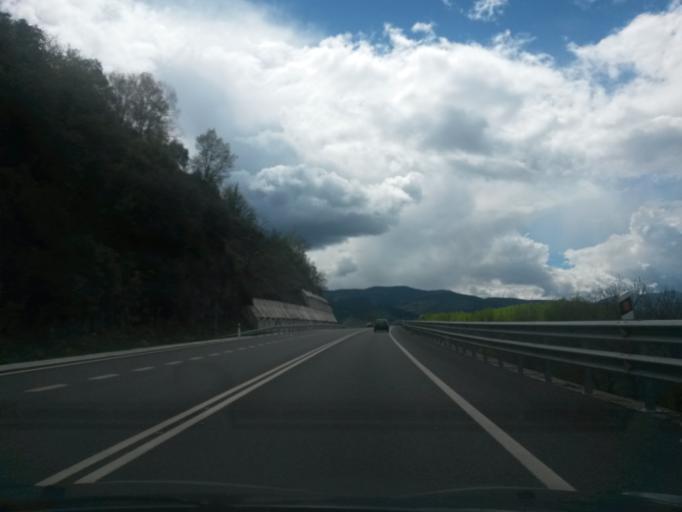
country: ES
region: Catalonia
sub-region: Provincia de Lleida
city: la Seu d'Urgell
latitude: 42.3683
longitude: 1.4554
